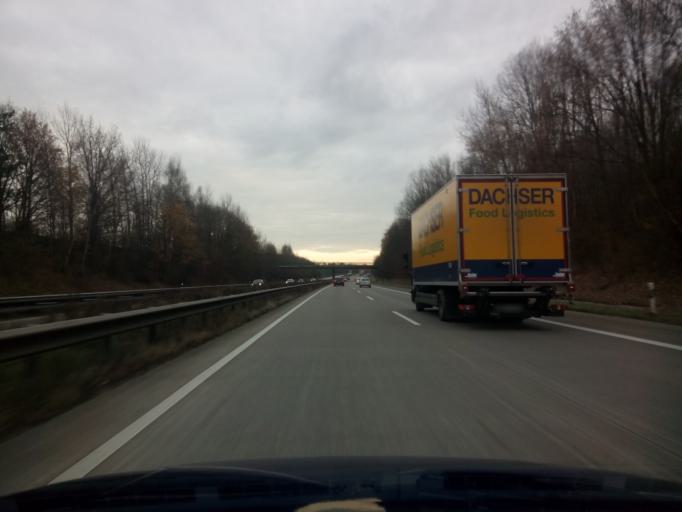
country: DE
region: Lower Saxony
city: Schiffdorf
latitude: 53.5170
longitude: 8.6275
